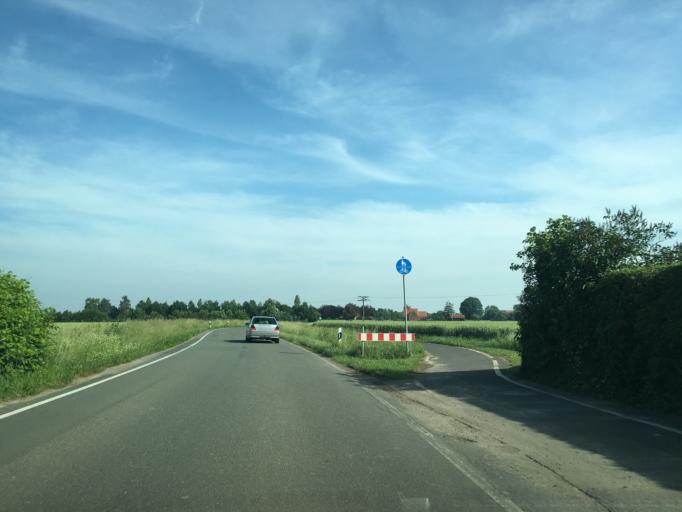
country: DE
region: North Rhine-Westphalia
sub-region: Regierungsbezirk Munster
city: Nordwalde
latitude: 52.1150
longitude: 7.4564
